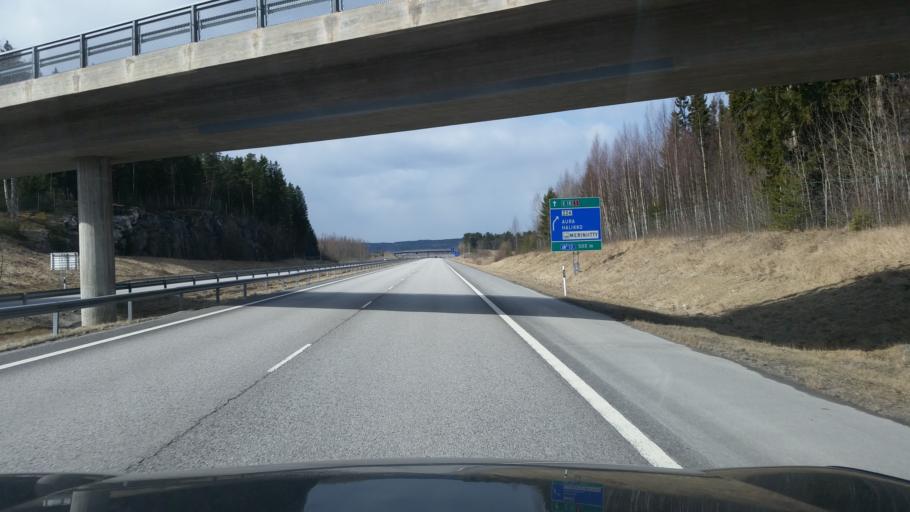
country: FI
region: Varsinais-Suomi
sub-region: Salo
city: Halikko
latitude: 60.4233
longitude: 23.0689
